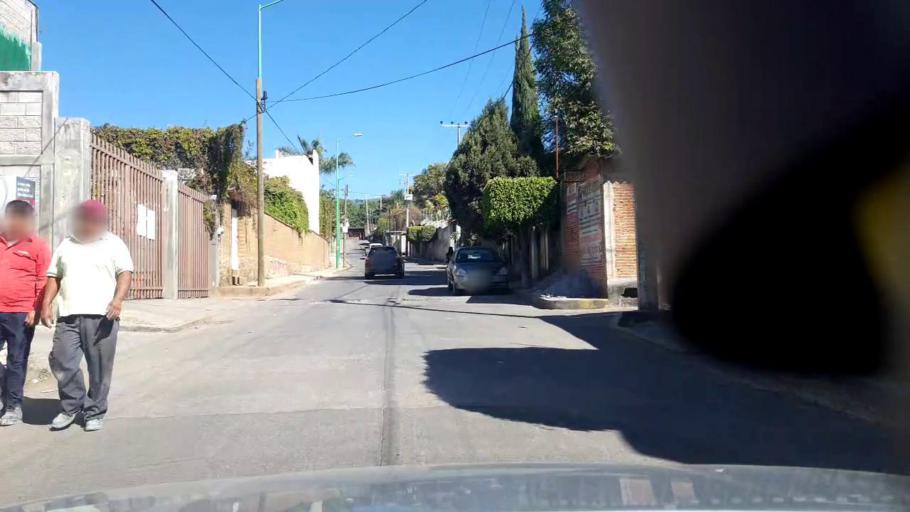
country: MX
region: Morelos
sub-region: Cuernavaca
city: Colonia los Cerritos
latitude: 18.9656
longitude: -99.2228
